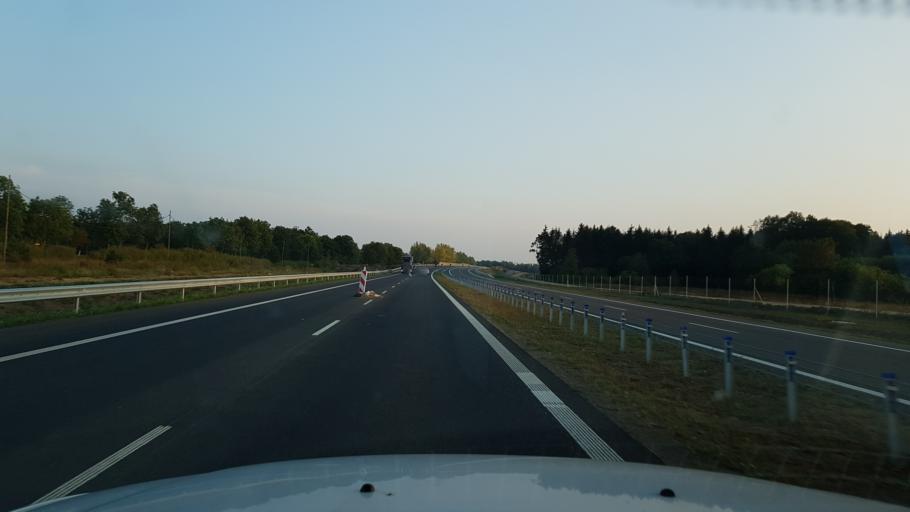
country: PL
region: West Pomeranian Voivodeship
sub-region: Powiat gryficki
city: Ploty
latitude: 53.7901
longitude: 15.2514
